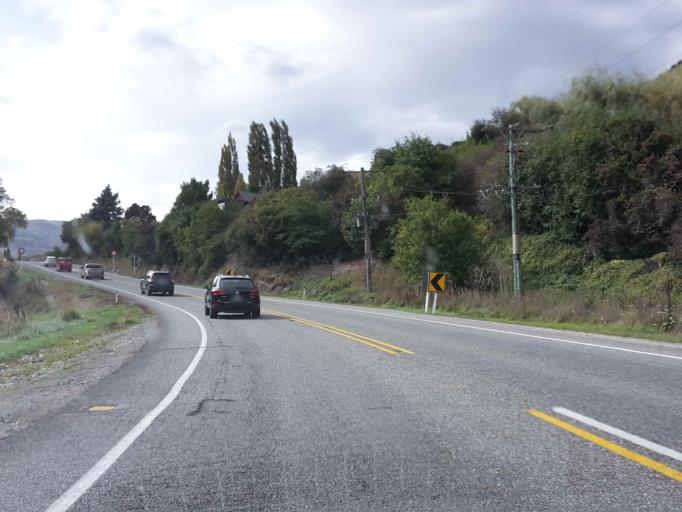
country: NZ
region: Otago
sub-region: Queenstown-Lakes District
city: Arrowtown
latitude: -44.9953
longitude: 168.8040
